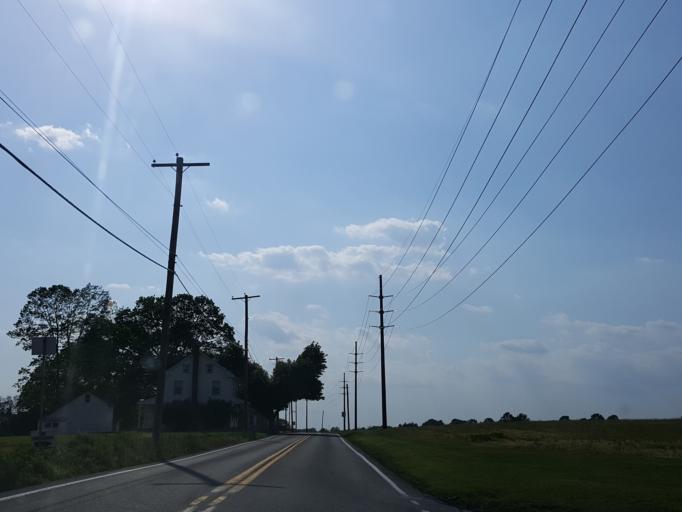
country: US
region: Pennsylvania
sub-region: Lebanon County
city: Campbelltown
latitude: 40.2603
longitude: -76.6173
